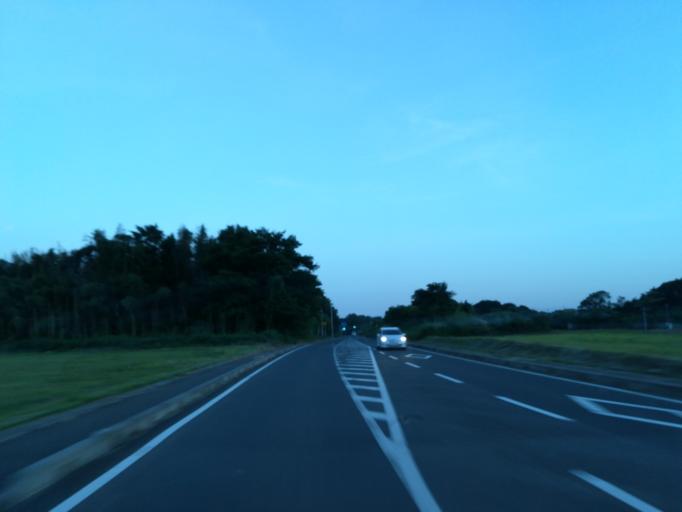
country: JP
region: Ibaraki
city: Makabe
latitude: 36.2678
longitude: 140.0584
